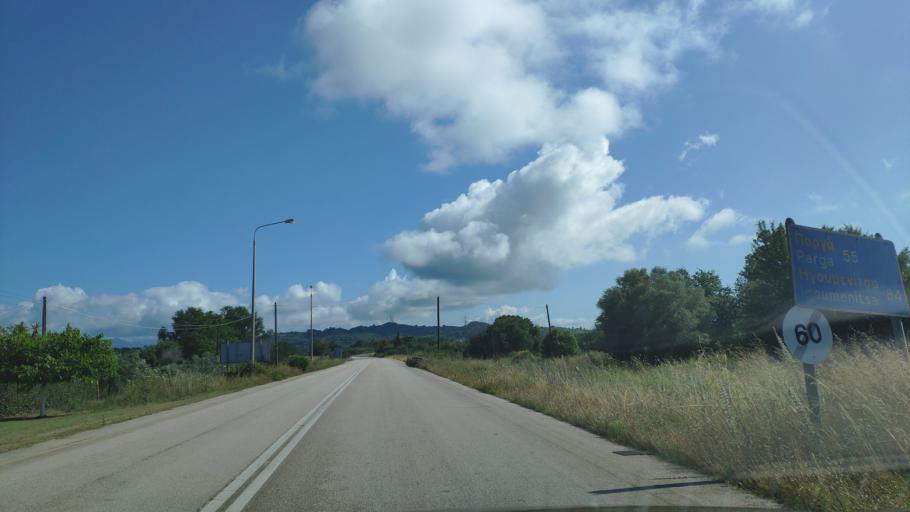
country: GR
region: Epirus
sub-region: Nomos Prevezis
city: Preveza
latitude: 39.0040
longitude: 20.7180
